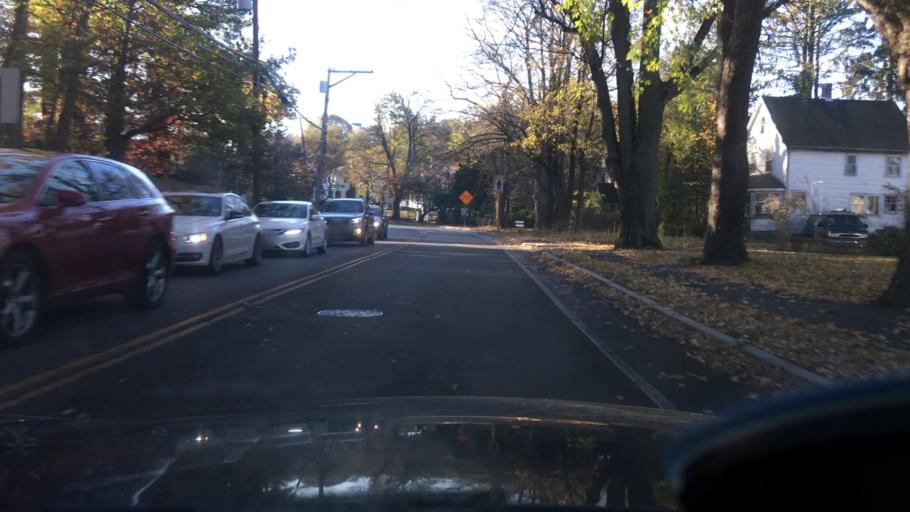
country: US
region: Massachusetts
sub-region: Norfolk County
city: Needham
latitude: 42.3144
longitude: -71.2464
